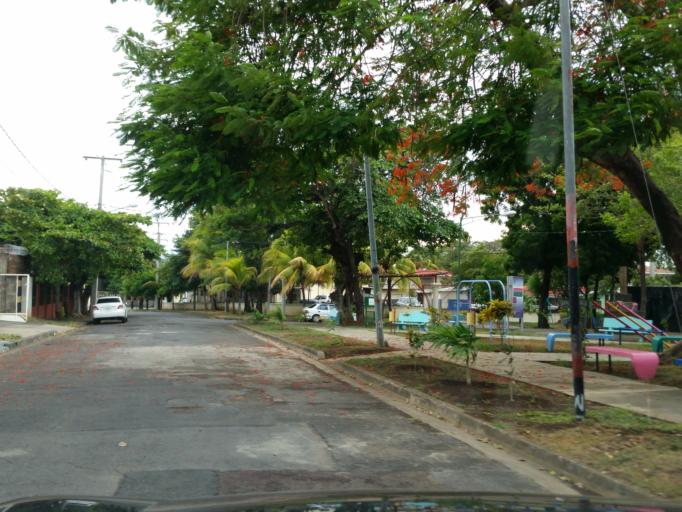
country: NI
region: Managua
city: Managua
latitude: 12.1484
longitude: -86.2850
